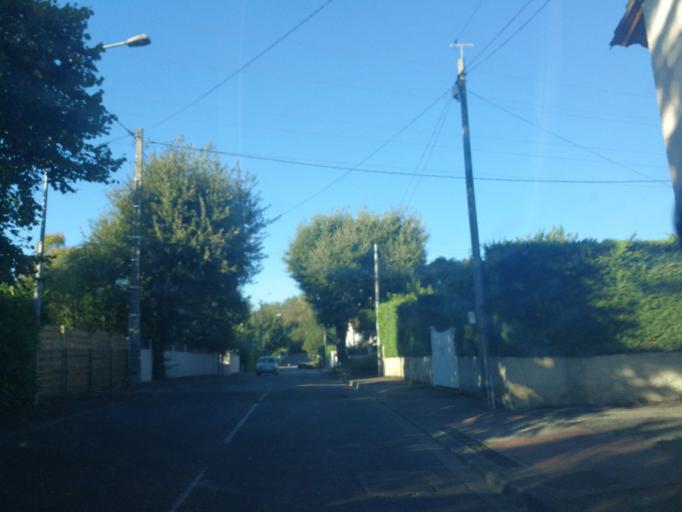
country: FR
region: Midi-Pyrenees
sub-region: Departement de la Haute-Garonne
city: Balma
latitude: 43.6151
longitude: 1.5033
